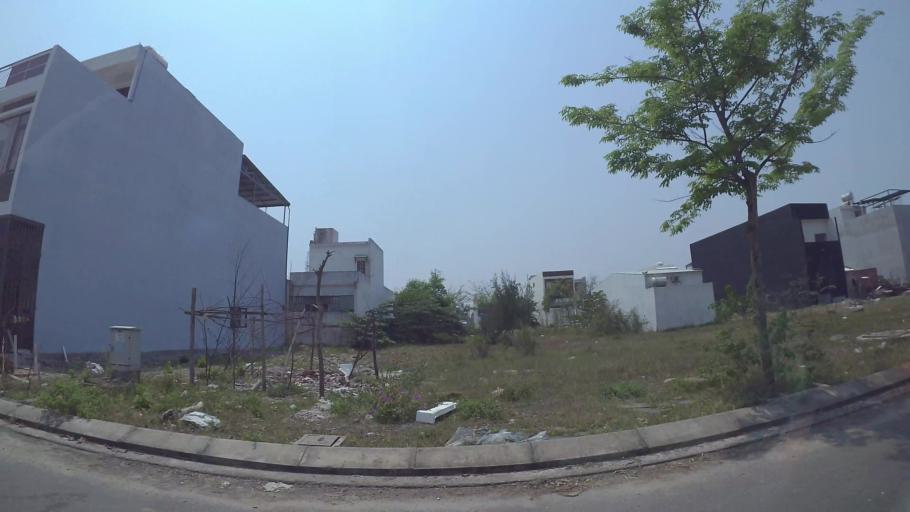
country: VN
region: Da Nang
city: Ngu Hanh Son
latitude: 15.9985
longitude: 108.2352
